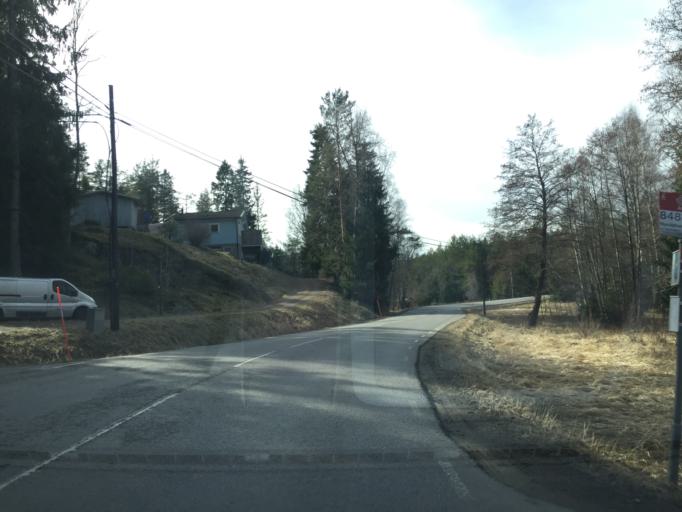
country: SE
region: Stockholm
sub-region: Haninge Kommun
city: Jordbro
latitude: 59.1102
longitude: 17.9971
